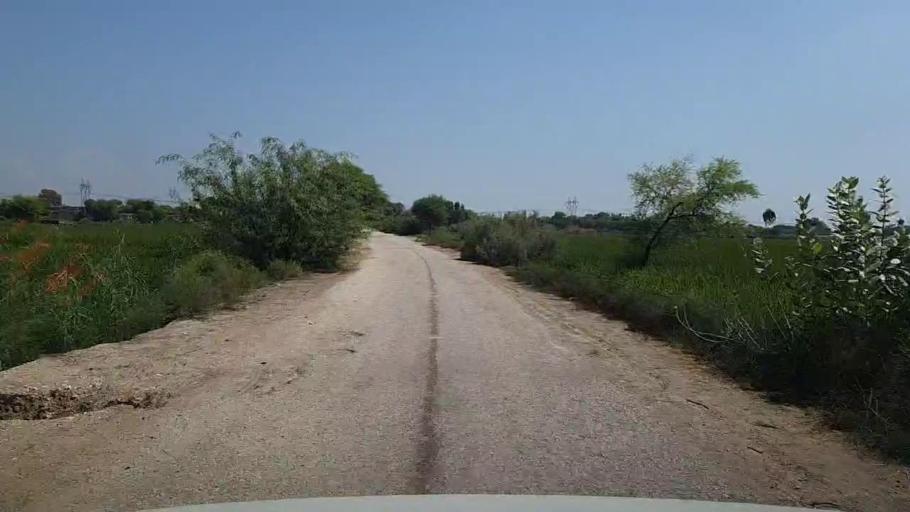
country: PK
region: Sindh
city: Kandhkot
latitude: 28.2908
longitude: 69.3519
